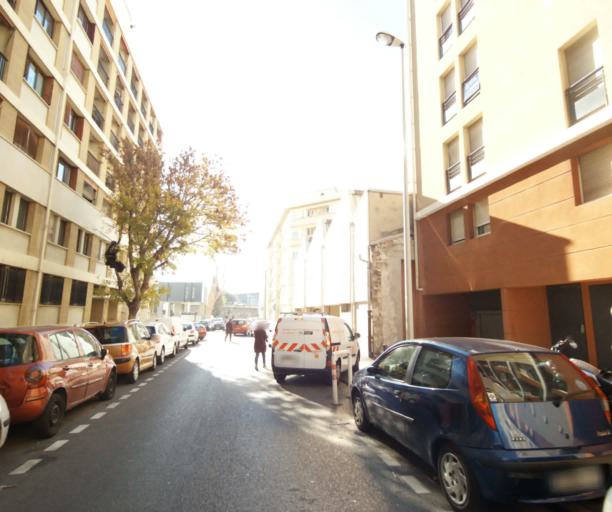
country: FR
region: Provence-Alpes-Cote d'Azur
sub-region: Departement des Bouches-du-Rhone
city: Marseille 05
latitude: 43.2851
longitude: 5.4016
